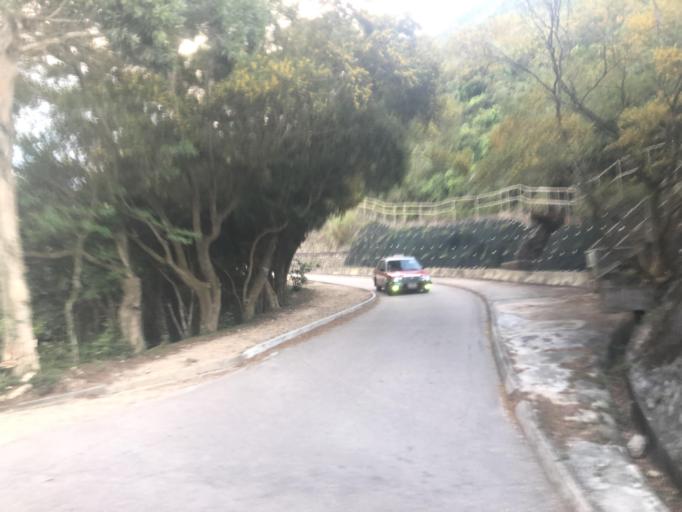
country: HK
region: Sai Kung
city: Sai Kung
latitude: 22.3676
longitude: 114.3456
